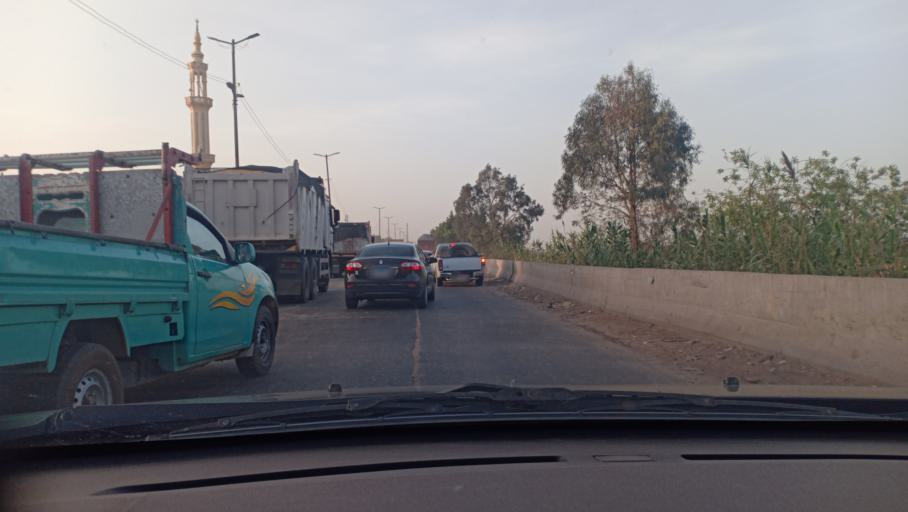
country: EG
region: Muhafazat al Minufiyah
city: Quwaysina
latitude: 30.5896
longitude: 31.2737
